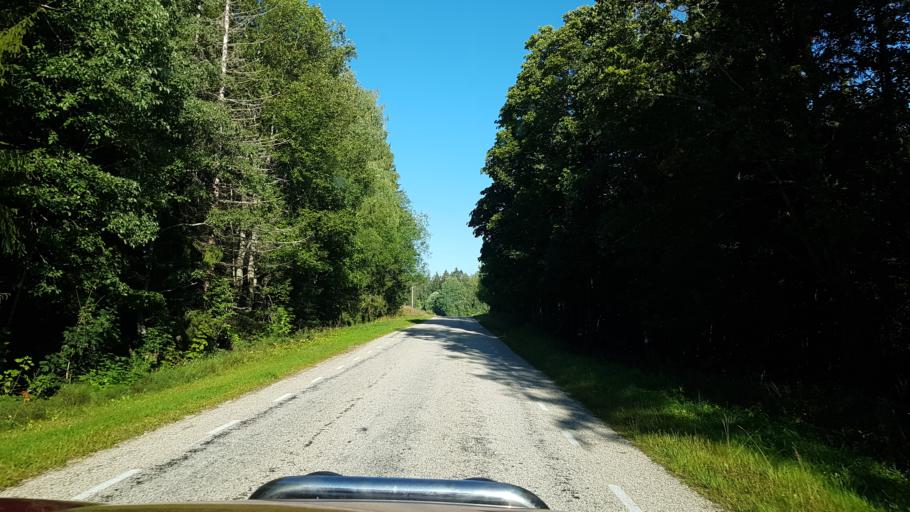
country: EE
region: Jogevamaa
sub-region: Tabivere vald
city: Tabivere
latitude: 58.6658
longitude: 26.7838
